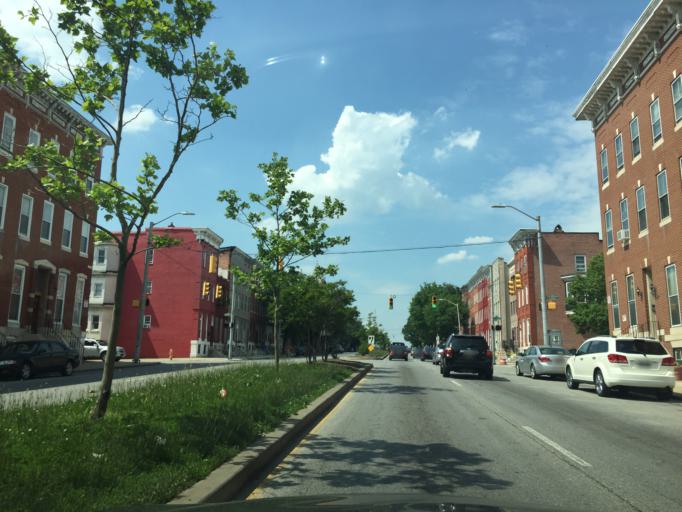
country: US
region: Maryland
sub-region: City of Baltimore
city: Baltimore
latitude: 39.2995
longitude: -76.6458
